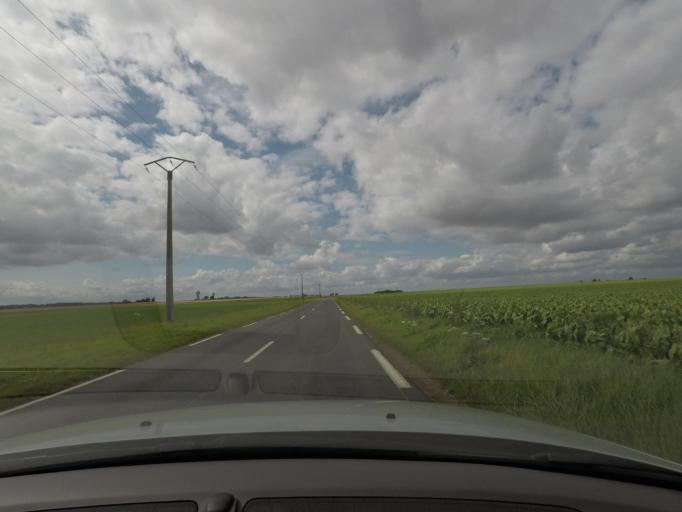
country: FR
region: Haute-Normandie
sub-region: Departement de l'Eure
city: Les Andelys
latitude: 49.2257
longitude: 1.4399
